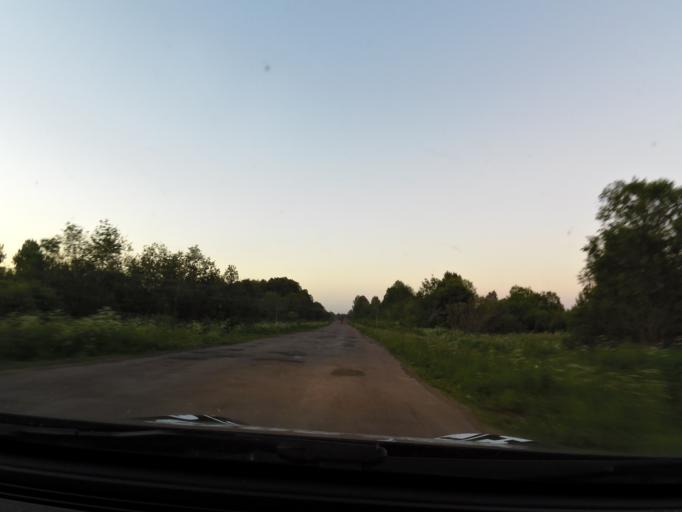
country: RU
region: Vologda
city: Vytegra
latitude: 60.8721
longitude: 36.0184
